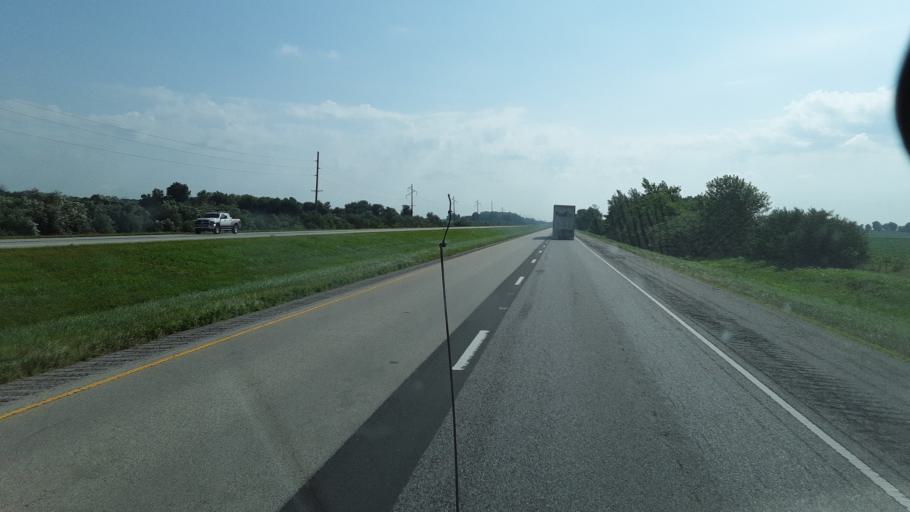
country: US
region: Illinois
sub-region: Fayette County
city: Vandalia
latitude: 38.9492
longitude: -89.1903
